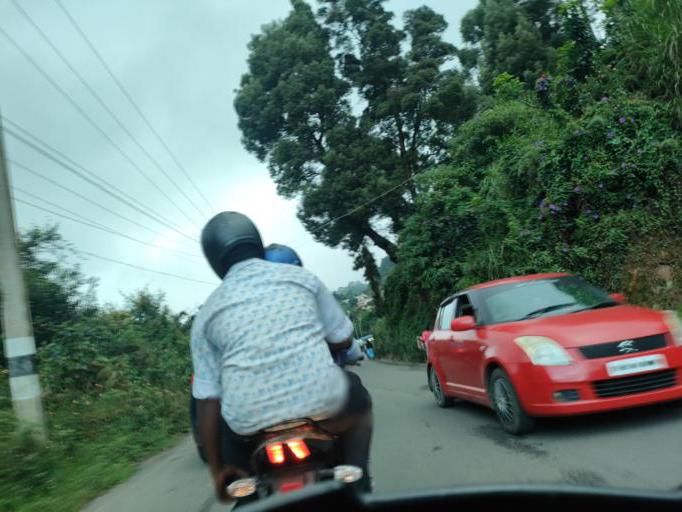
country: IN
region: Tamil Nadu
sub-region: Dindigul
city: Kodaikanal
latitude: 10.2378
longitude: 77.5076
